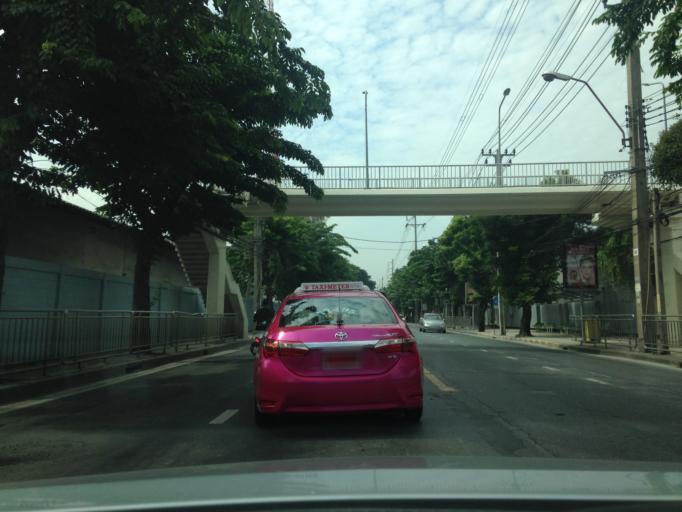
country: TH
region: Bangkok
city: Bang Phlat
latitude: 13.7963
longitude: 100.5205
